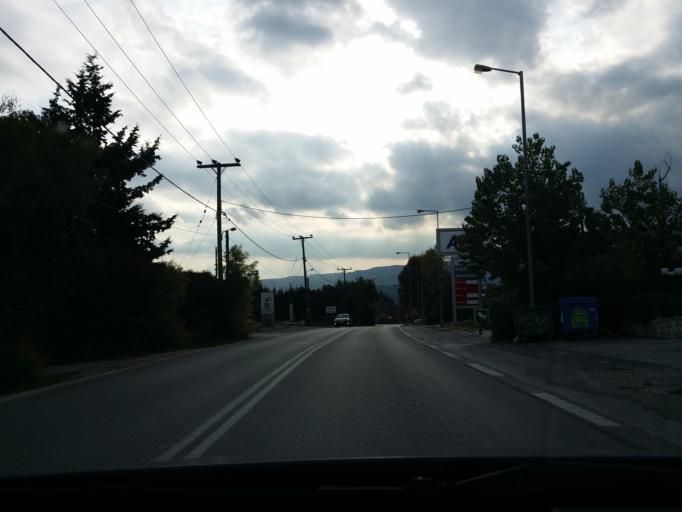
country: GR
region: Attica
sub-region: Nomarchia Anatolikis Attikis
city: Kapandriti
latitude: 38.2107
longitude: 23.8729
